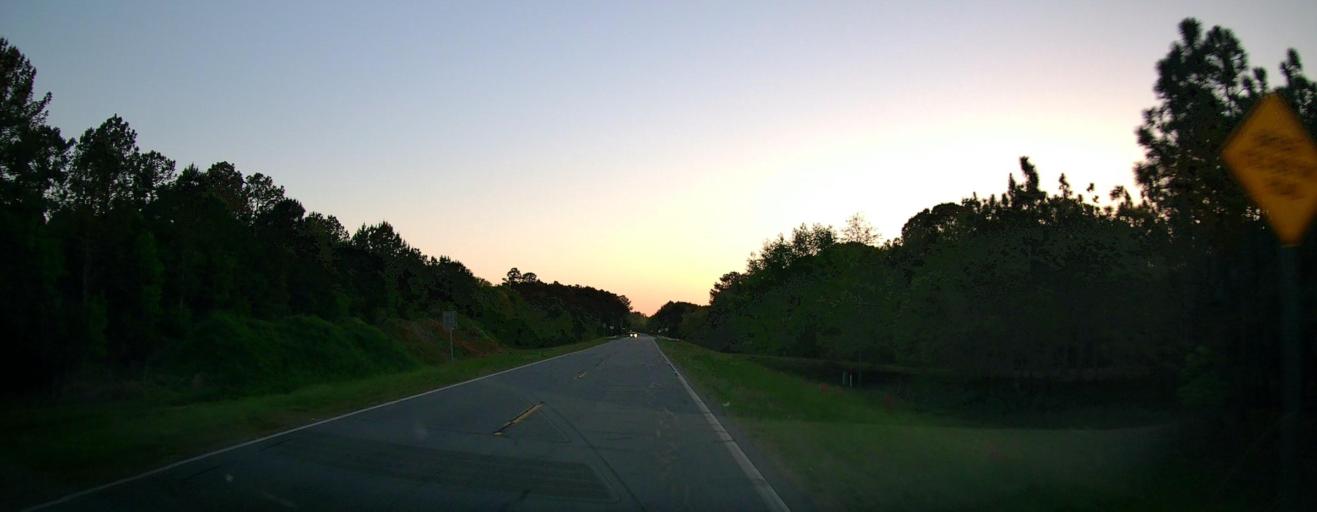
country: US
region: Georgia
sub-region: Wilcox County
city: Rochelle
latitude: 31.8167
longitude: -83.4722
